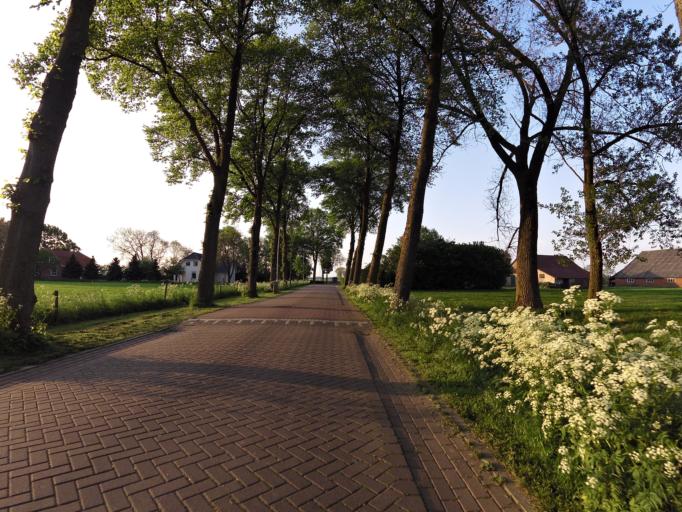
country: NL
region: Gelderland
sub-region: Gemeente Montferland
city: s-Heerenberg
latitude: 51.8577
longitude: 6.3148
